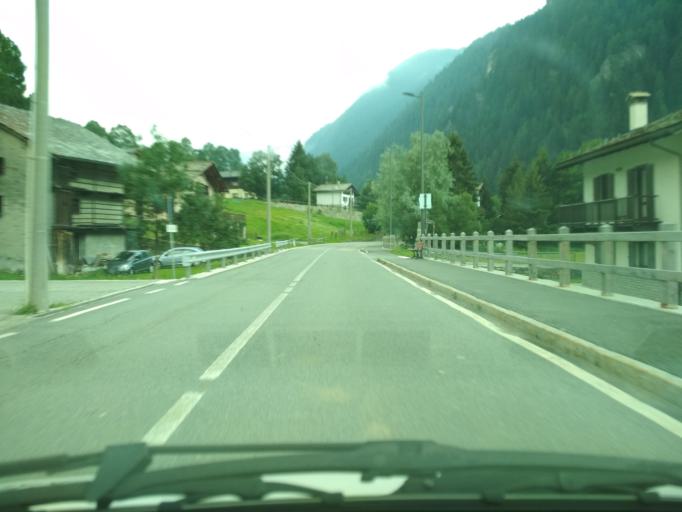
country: IT
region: Aosta Valley
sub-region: Valle d'Aosta
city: Gressoney-Saint-Jean
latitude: 45.7568
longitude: 7.8410
